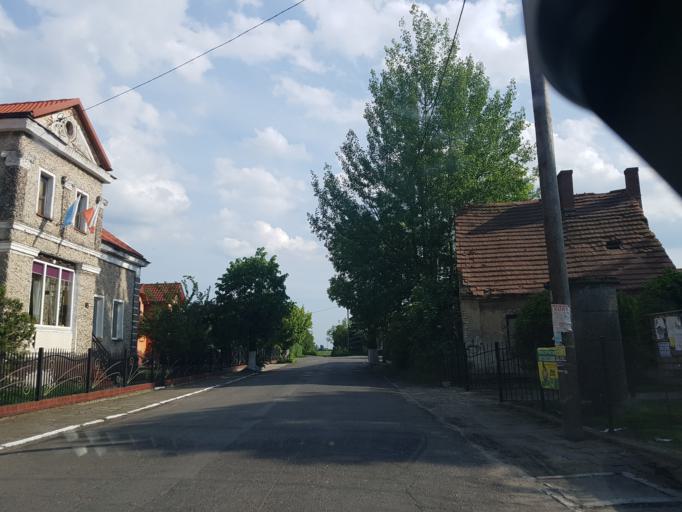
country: PL
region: Lower Silesian Voivodeship
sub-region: Powiat strzelinski
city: Wiazow
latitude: 50.8670
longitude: 17.1564
